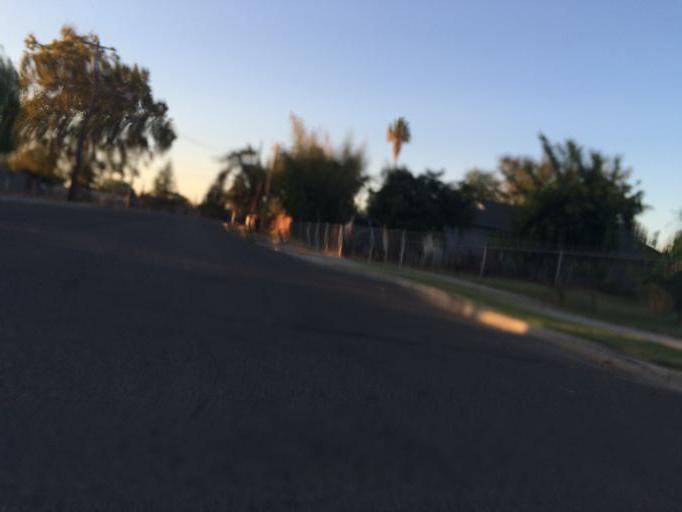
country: US
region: California
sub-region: Fresno County
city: Fresno
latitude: 36.7568
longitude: -119.7567
